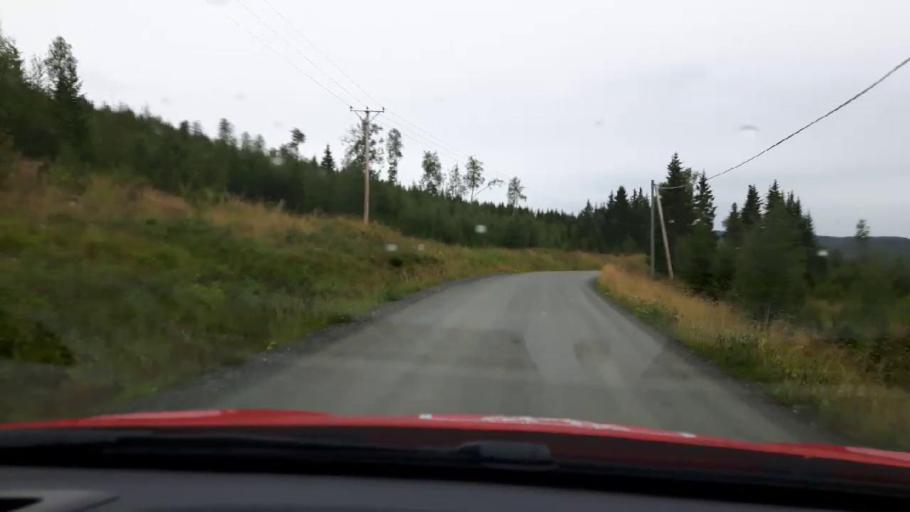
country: SE
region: Jaemtland
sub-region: Are Kommun
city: Are
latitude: 63.4179
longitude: 12.8263
